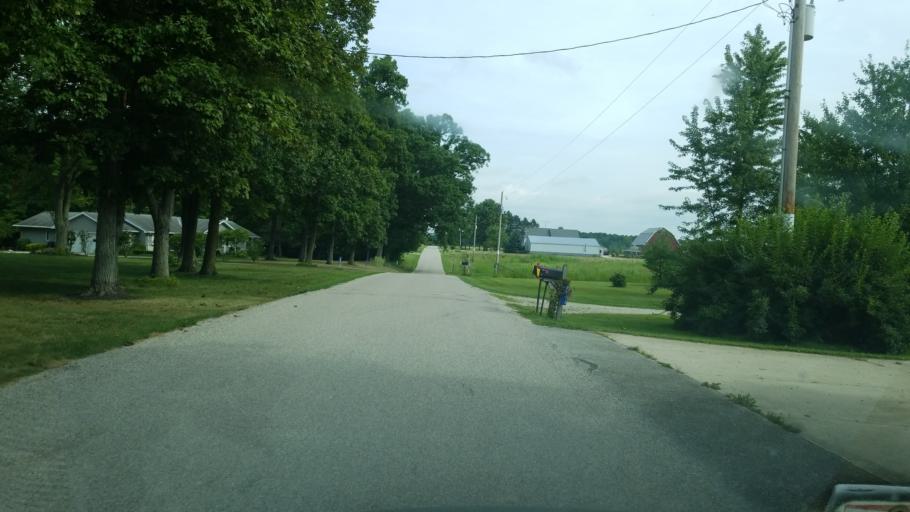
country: US
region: Ohio
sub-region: Seneca County
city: Tiffin
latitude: 41.1613
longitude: -83.0946
